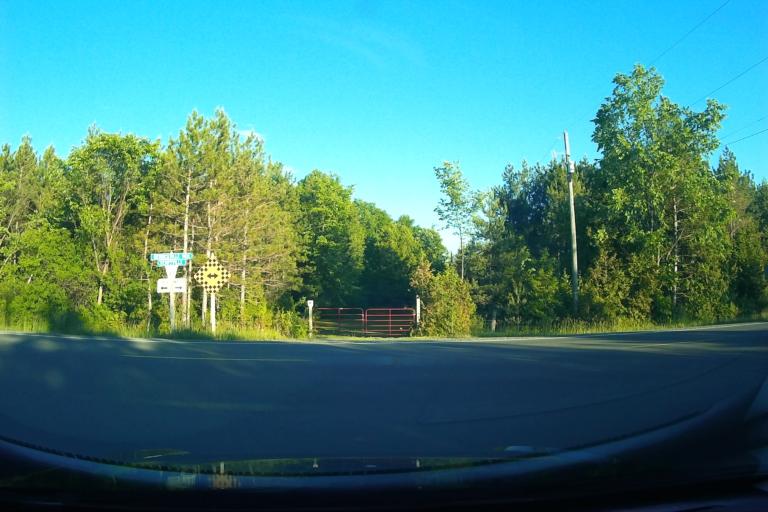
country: CA
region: Ontario
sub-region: Lanark County
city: Smiths Falls
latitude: 44.9604
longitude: -75.7685
